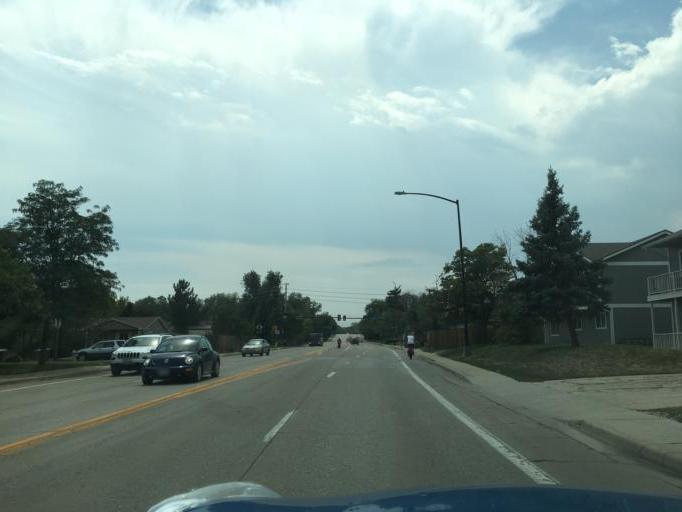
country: US
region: Colorado
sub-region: Boulder County
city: Boulder
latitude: 40.0049
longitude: -105.2531
